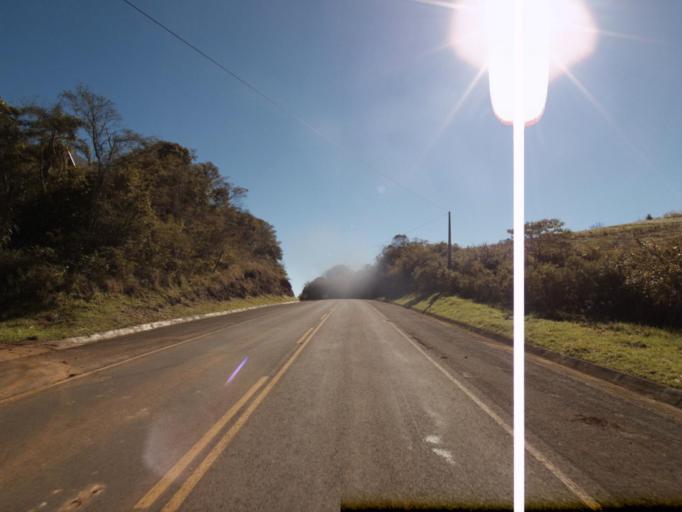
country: AR
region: Misiones
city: Bernardo de Irigoyen
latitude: -26.6820
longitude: -53.5529
